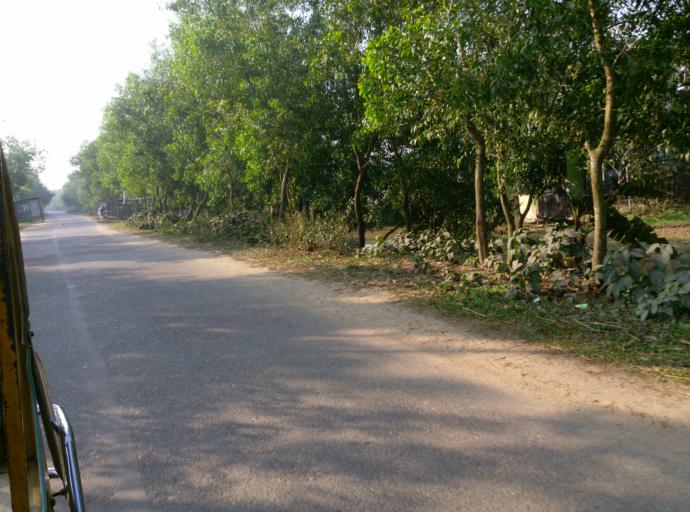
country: BD
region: Dhaka
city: Netrakona
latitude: 25.1485
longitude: 90.6593
